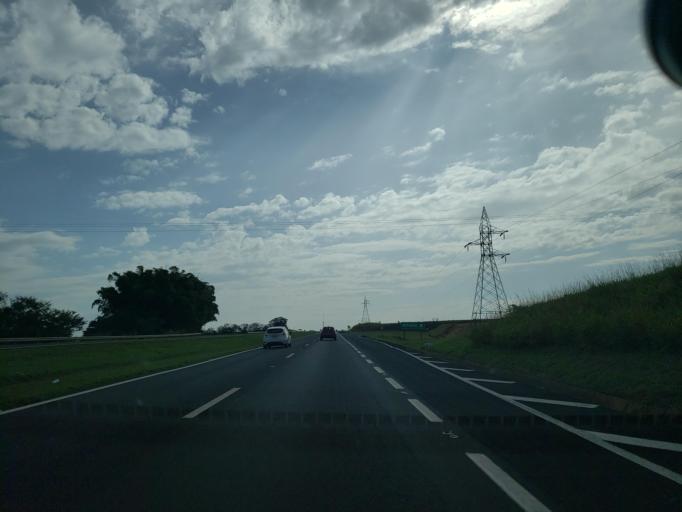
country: BR
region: Sao Paulo
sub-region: Lins
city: Lins
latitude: -21.7381
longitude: -49.7020
